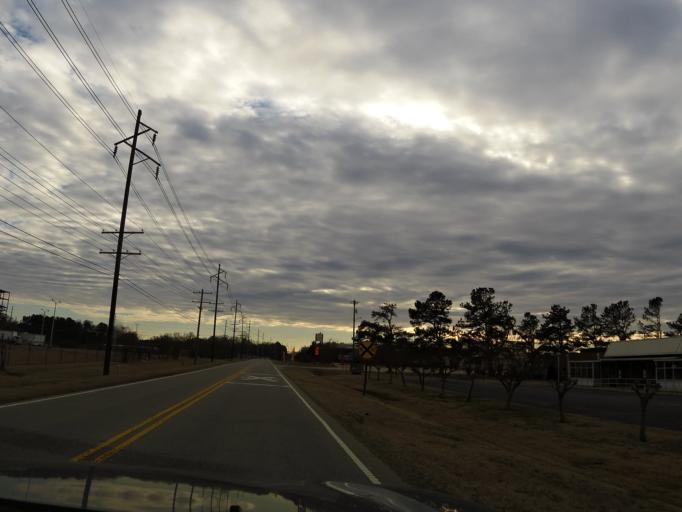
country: US
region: North Carolina
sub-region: Nash County
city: Rocky Mount
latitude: 35.9658
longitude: -77.7820
